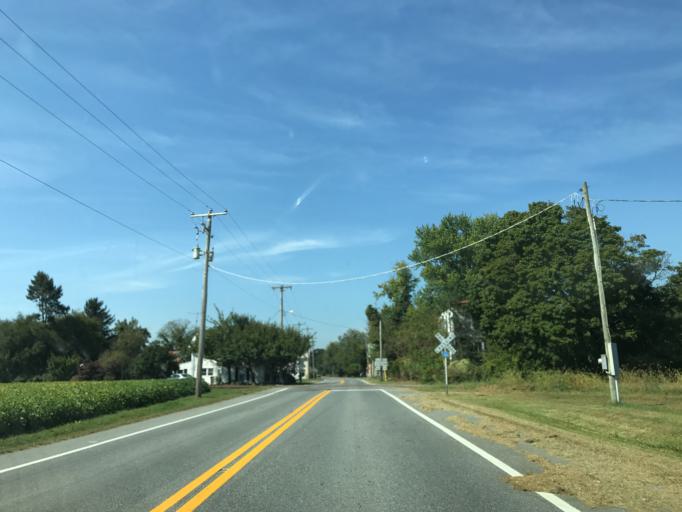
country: US
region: Delaware
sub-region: New Castle County
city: Townsend
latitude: 39.3090
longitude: -75.8235
